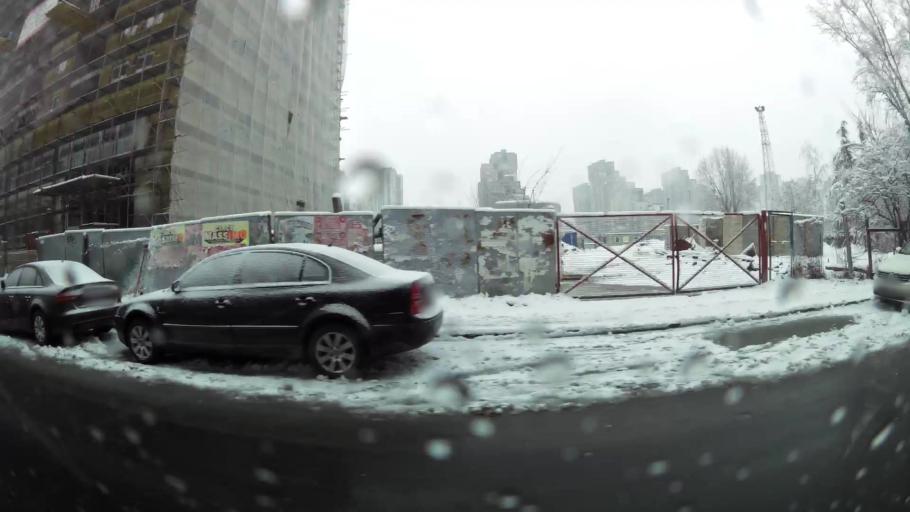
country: RS
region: Central Serbia
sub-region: Belgrade
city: Cukarica
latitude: 44.7993
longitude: 20.3770
